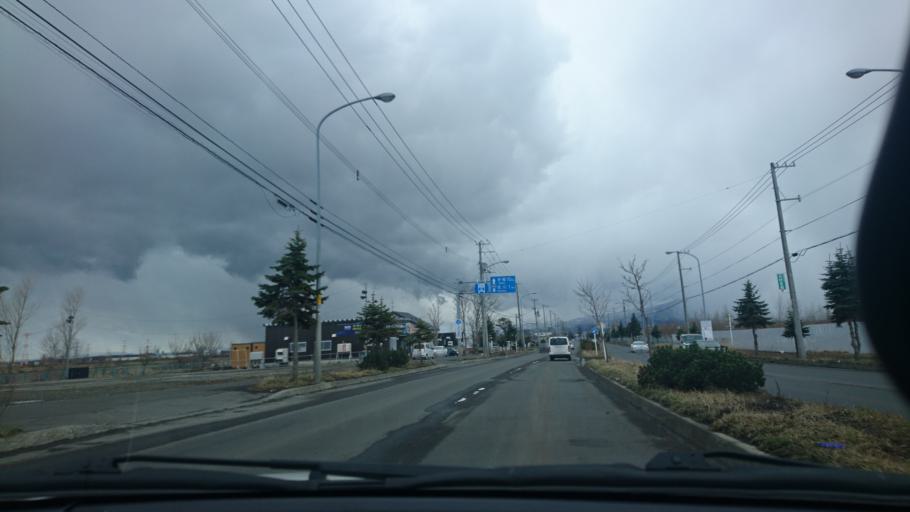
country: JP
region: Hokkaido
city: Ishikari
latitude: 43.1821
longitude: 141.3227
